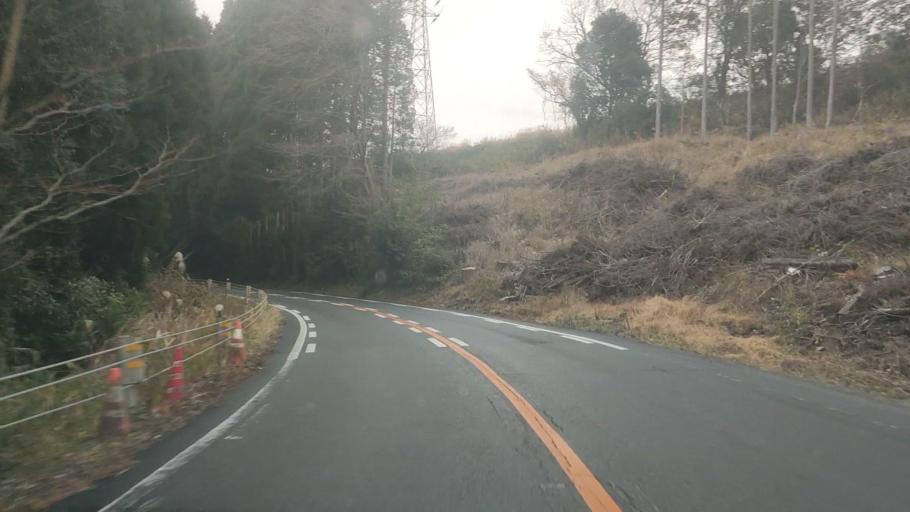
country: JP
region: Kumamoto
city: Aso
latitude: 32.8971
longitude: 130.9985
